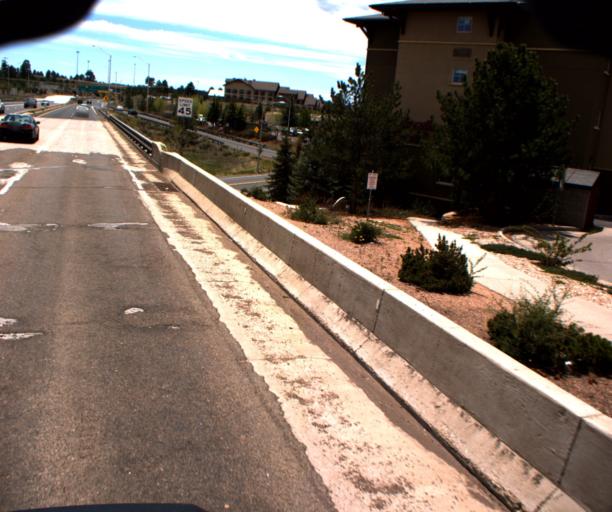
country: US
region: Arizona
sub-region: Coconino County
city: Flagstaff
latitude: 35.1780
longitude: -111.6614
